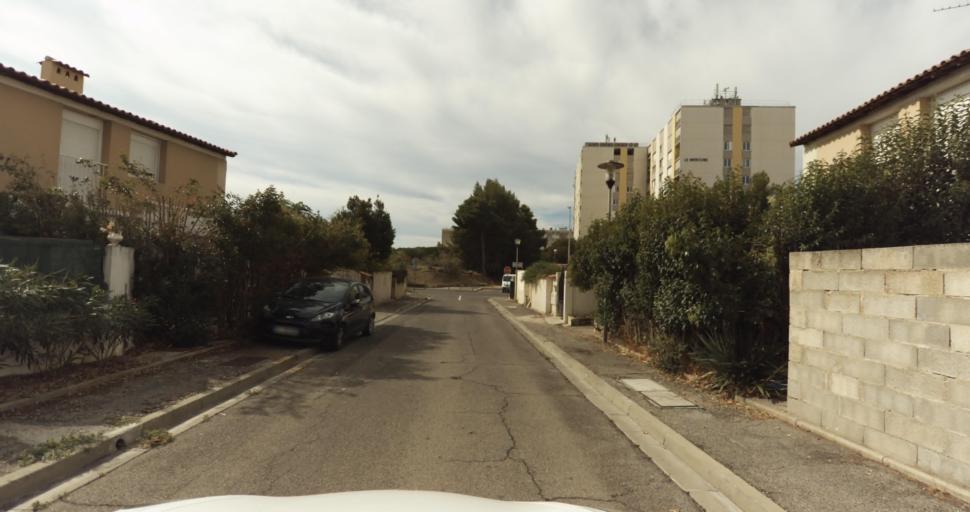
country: FR
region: Provence-Alpes-Cote d'Azur
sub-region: Departement des Bouches-du-Rhone
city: Miramas
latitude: 43.5927
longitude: 5.0076
